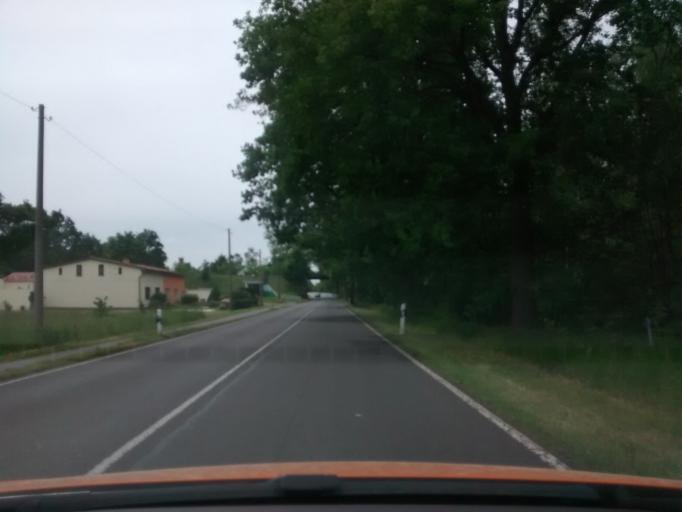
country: DE
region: Brandenburg
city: Juterbog
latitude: 52.0144
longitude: 13.0993
